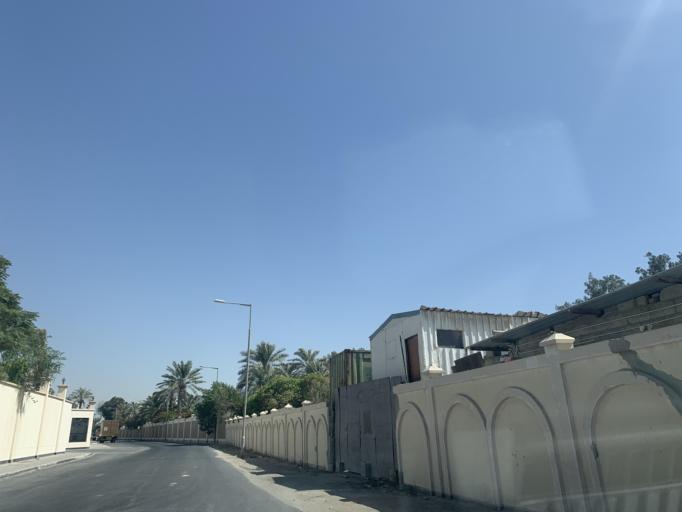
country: BH
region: Manama
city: Jidd Hafs
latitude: 26.2249
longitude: 50.4994
